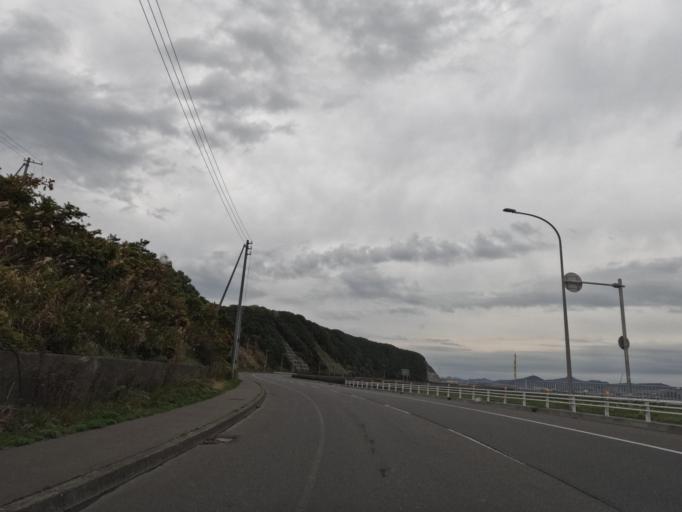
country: JP
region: Hokkaido
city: Muroran
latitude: 42.3768
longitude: 140.9095
